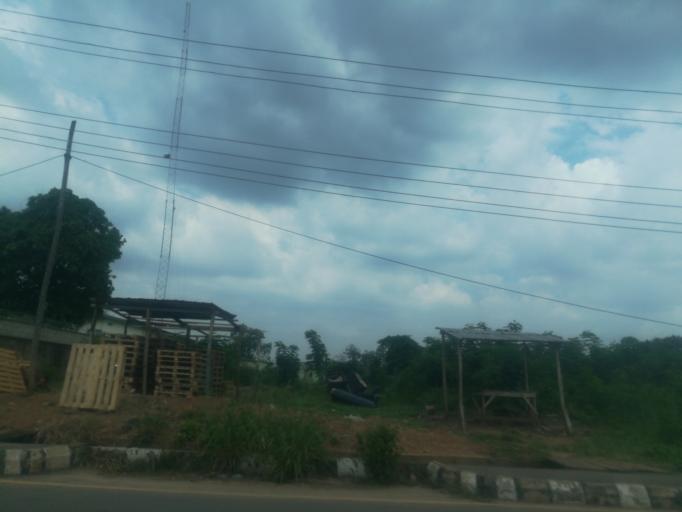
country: NG
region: Oyo
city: Ibadan
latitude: 7.3989
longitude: 3.8755
